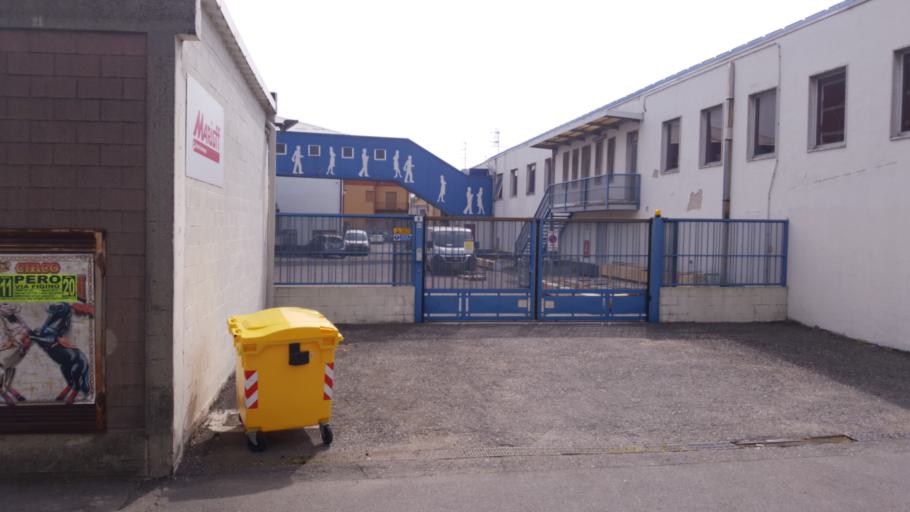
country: IT
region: Lombardy
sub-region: Citta metropolitana di Milano
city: Rho
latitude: 45.5183
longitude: 9.0686
